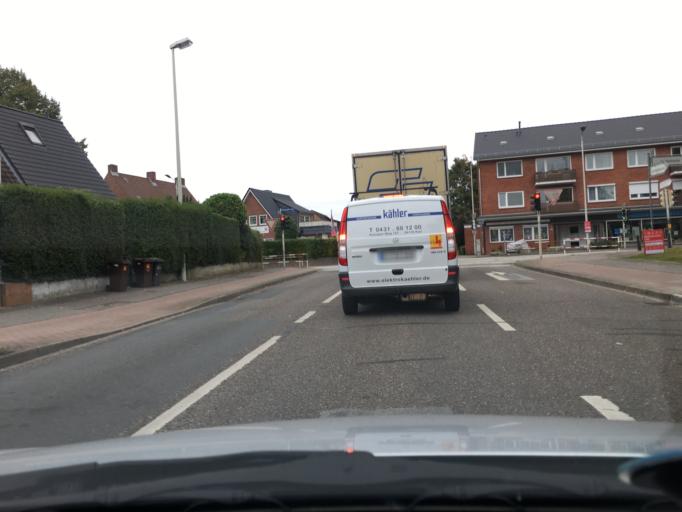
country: DE
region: Schleswig-Holstein
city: Kronshagen
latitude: 54.3384
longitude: 10.0876
